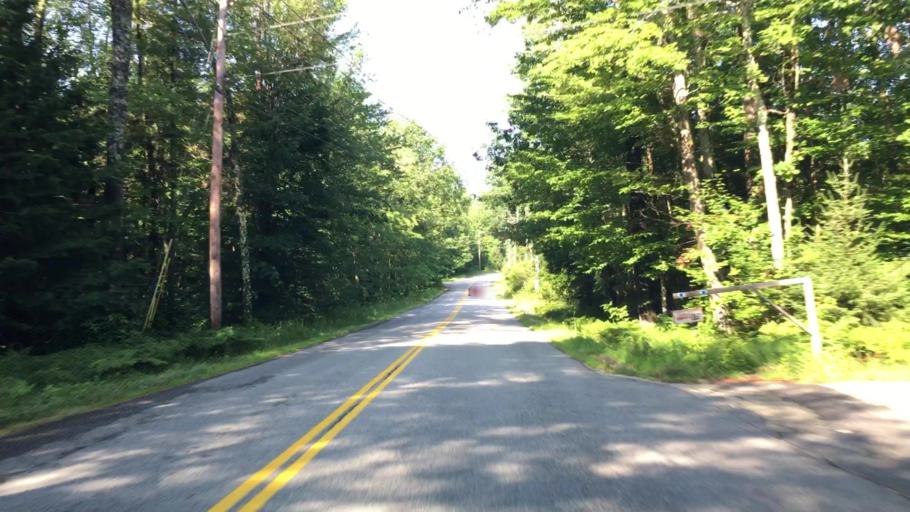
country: US
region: Maine
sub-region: Androscoggin County
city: Minot
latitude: 44.0435
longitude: -70.3141
